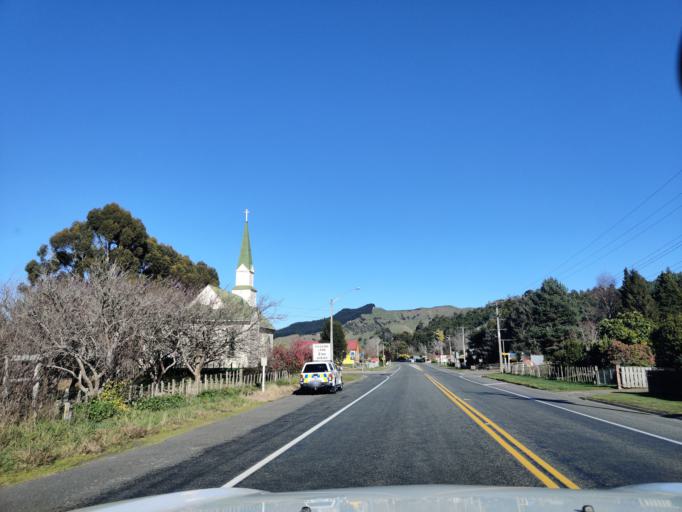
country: NZ
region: Manawatu-Wanganui
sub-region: Ruapehu District
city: Waiouru
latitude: -39.8083
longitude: 175.7915
